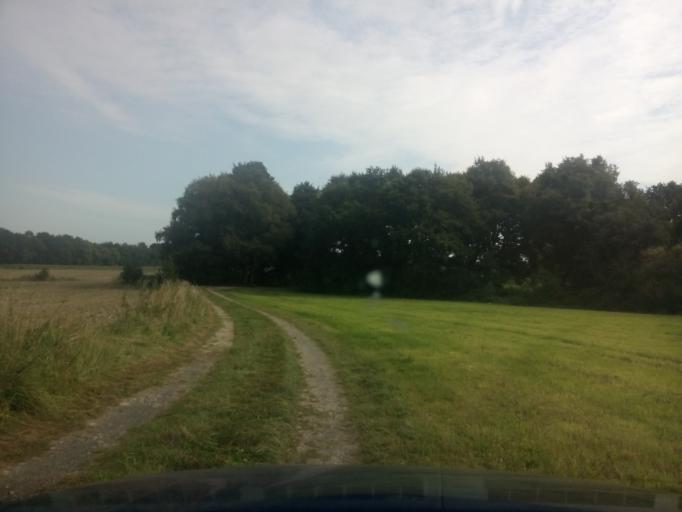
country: DE
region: Lower Saxony
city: Osterholz-Scharmbeck
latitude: 53.2364
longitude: 8.7709
